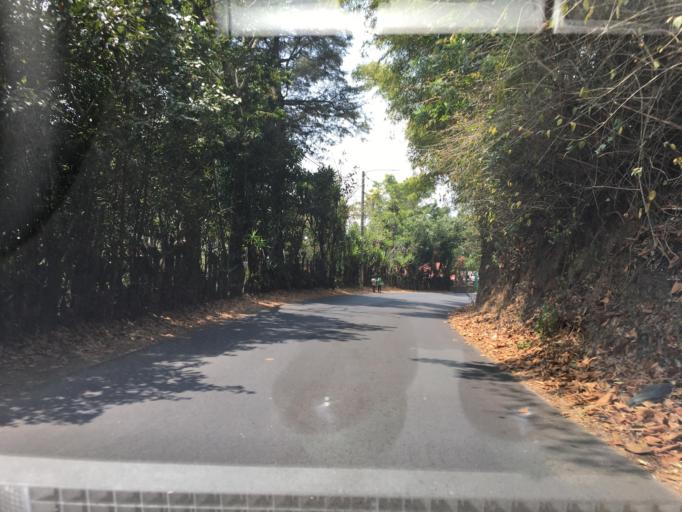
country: GT
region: Guatemala
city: Villa Canales
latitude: 14.3924
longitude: -90.5475
